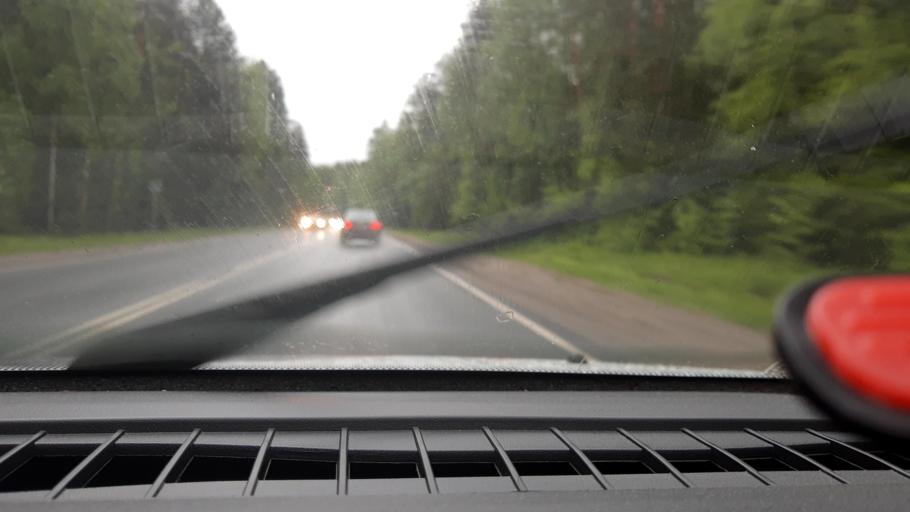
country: RU
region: Nizjnij Novgorod
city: Semenov
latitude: 56.7411
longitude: 44.3439
